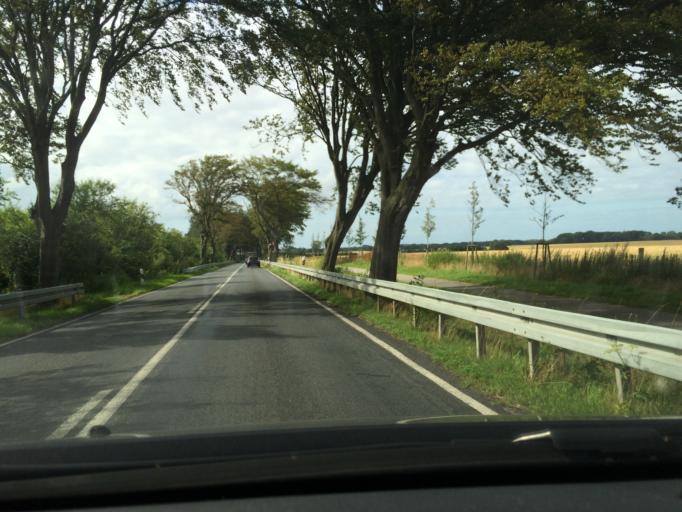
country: DE
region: Mecklenburg-Vorpommern
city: Kramerhof
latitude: 54.3542
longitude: 13.0407
